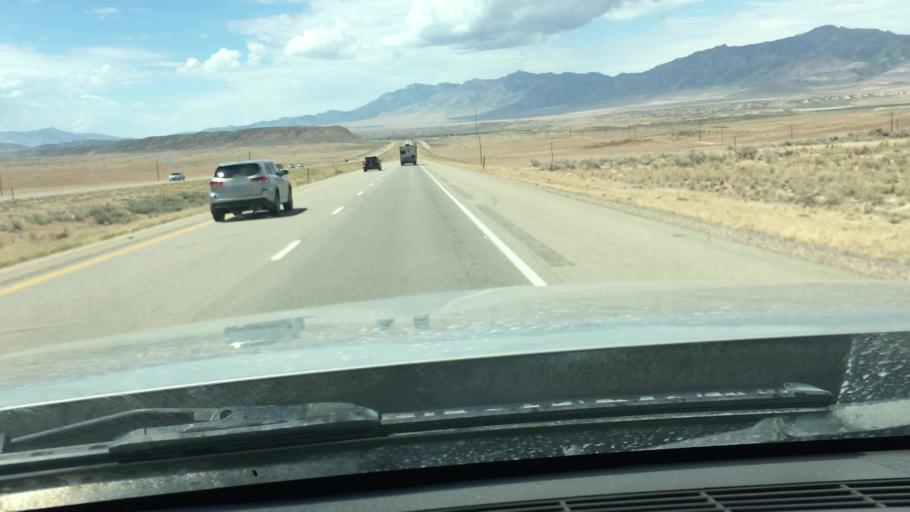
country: US
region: Utah
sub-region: Juab County
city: Nephi
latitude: 39.4636
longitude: -112.0015
